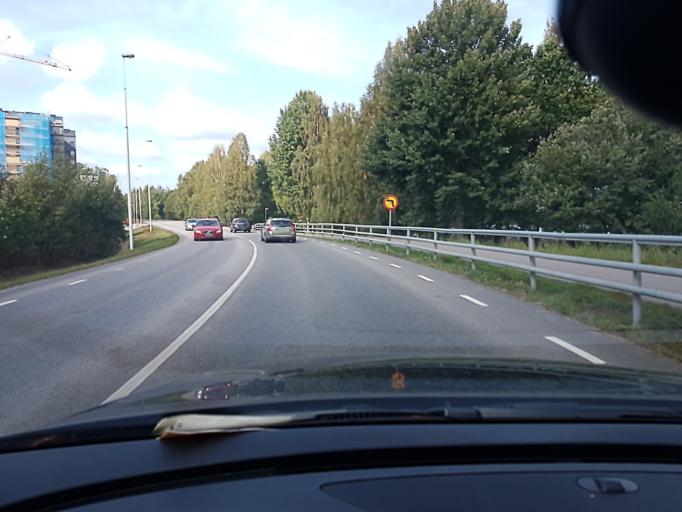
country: SE
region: Kronoberg
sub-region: Vaxjo Kommun
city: Vaexjoe
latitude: 56.8606
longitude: 14.8098
